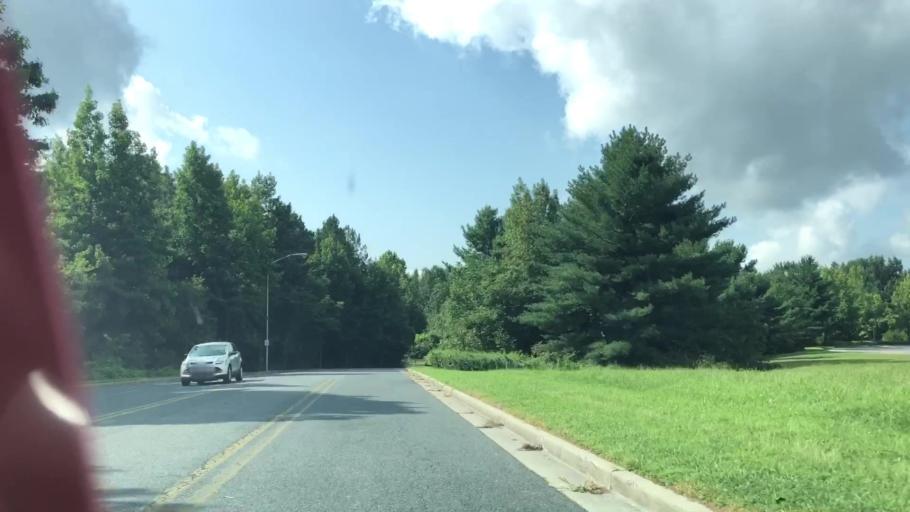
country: US
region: Maryland
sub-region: Wicomico County
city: Salisbury
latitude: 38.3972
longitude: -75.5628
